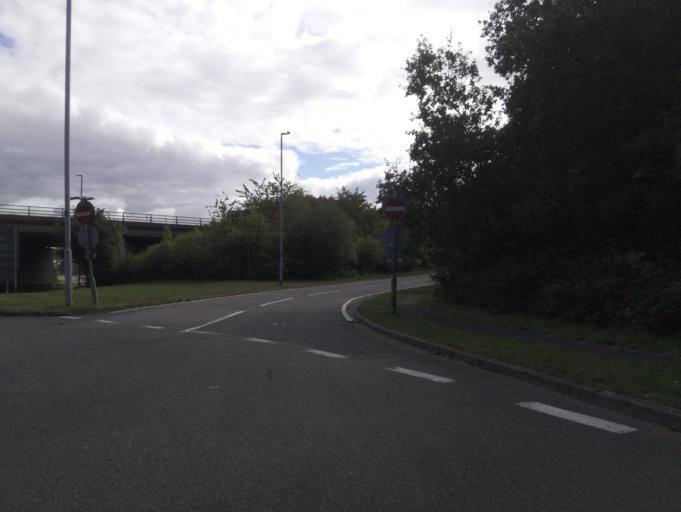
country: GB
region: England
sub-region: Leicestershire
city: Ashby de la Zouch
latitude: 52.7266
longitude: -1.4887
